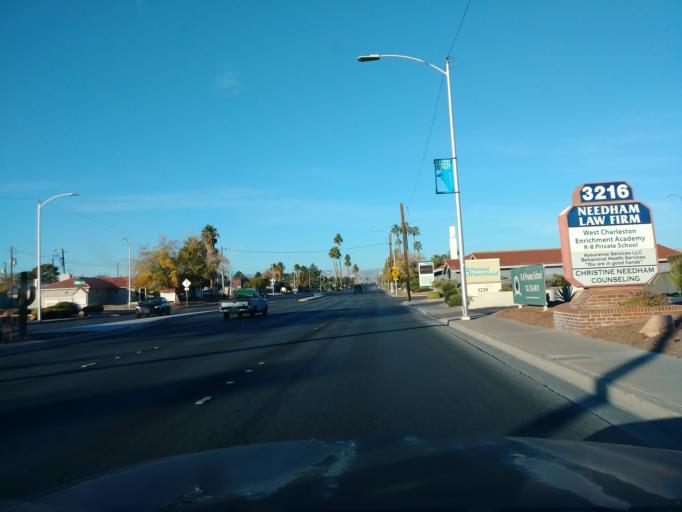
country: US
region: Nevada
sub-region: Clark County
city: Las Vegas
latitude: 36.1591
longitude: -115.1855
